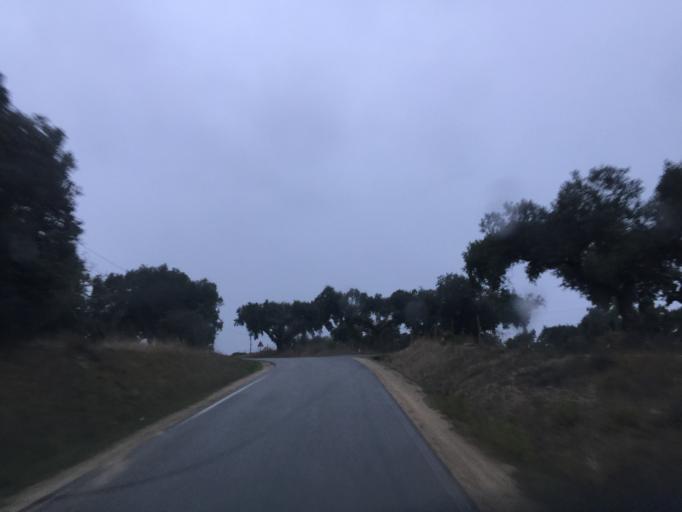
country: PT
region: Portalegre
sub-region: Avis
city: Avis
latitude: 39.0512
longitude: -7.9026
